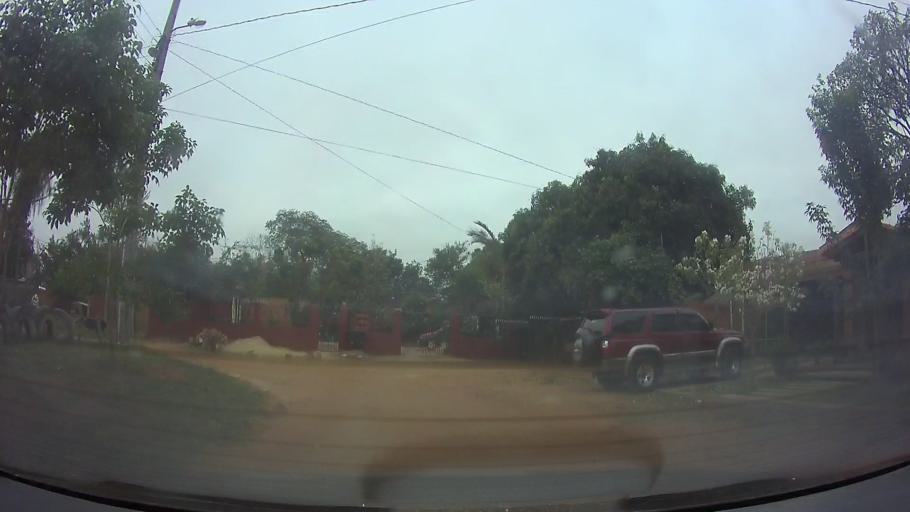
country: PY
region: Central
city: Limpio
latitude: -25.1528
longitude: -57.4554
